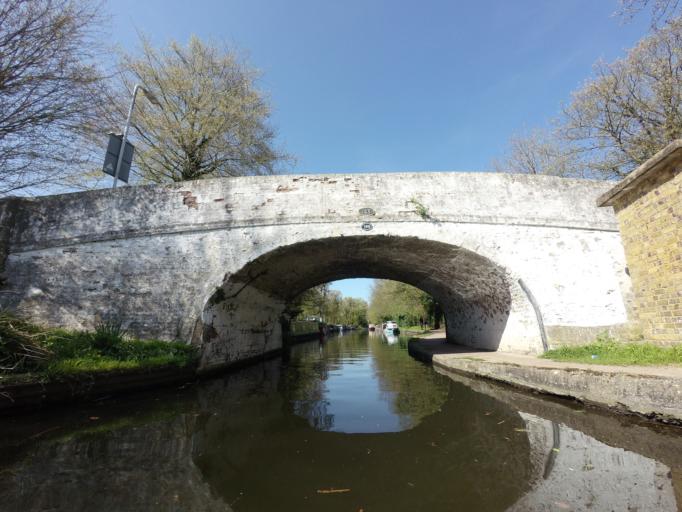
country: GB
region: England
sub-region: Greater London
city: Uxbridge
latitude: 51.5250
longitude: -0.4860
